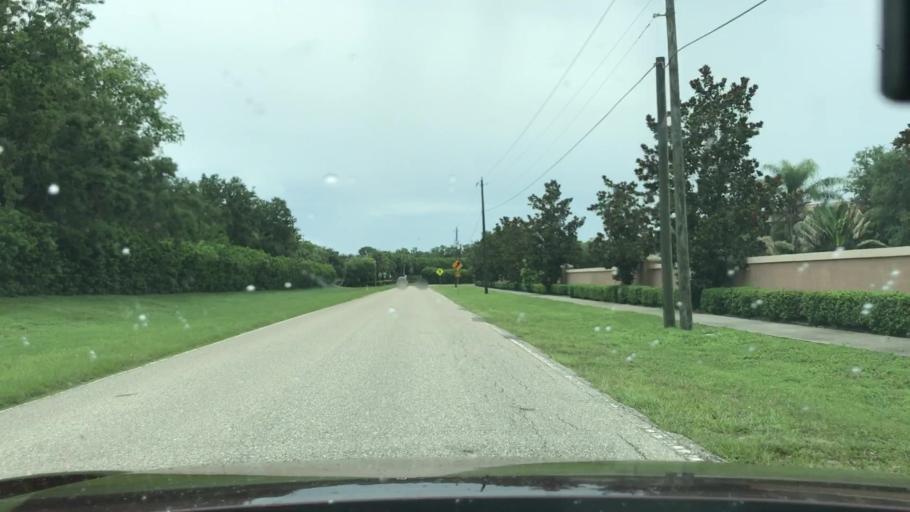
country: US
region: Florida
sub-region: Sarasota County
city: Lake Sarasota
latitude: 27.3161
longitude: -82.4023
